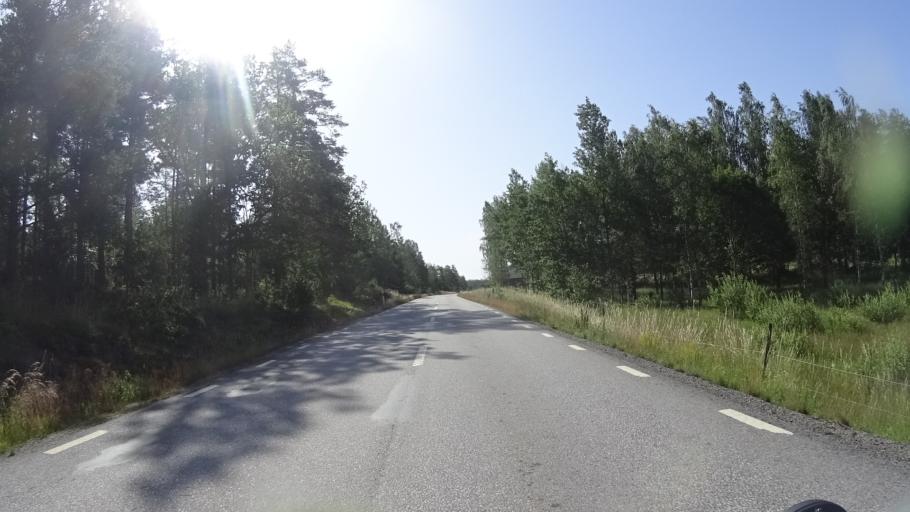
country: SE
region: OEstergoetland
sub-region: Atvidabergs Kommun
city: Atvidaberg
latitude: 58.0924
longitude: 16.1320
